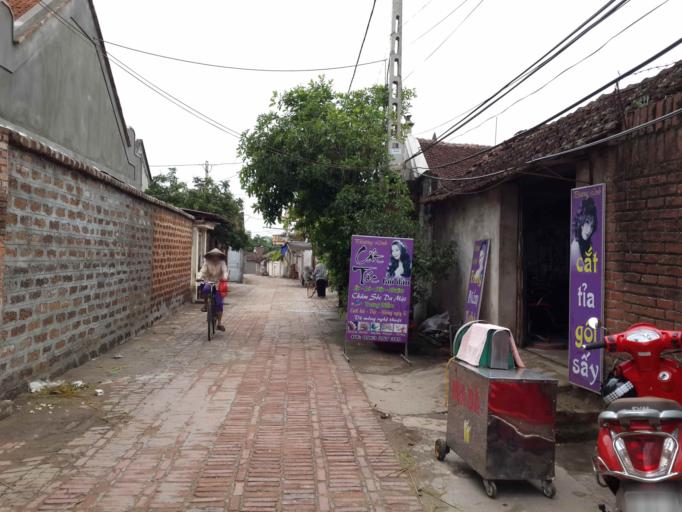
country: VN
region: Ha Noi
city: Son Tay
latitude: 21.1578
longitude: 105.4698
